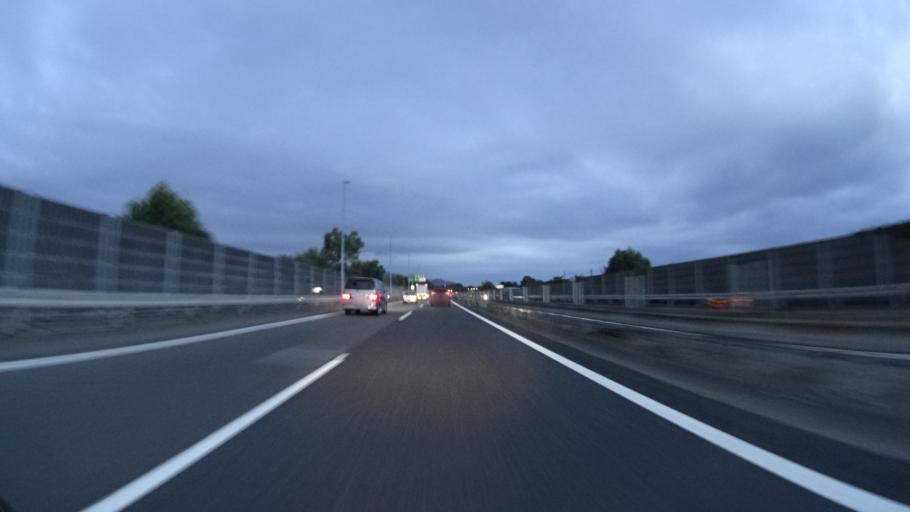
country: JP
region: Shiga Prefecture
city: Hikone
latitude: 35.2324
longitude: 136.2828
